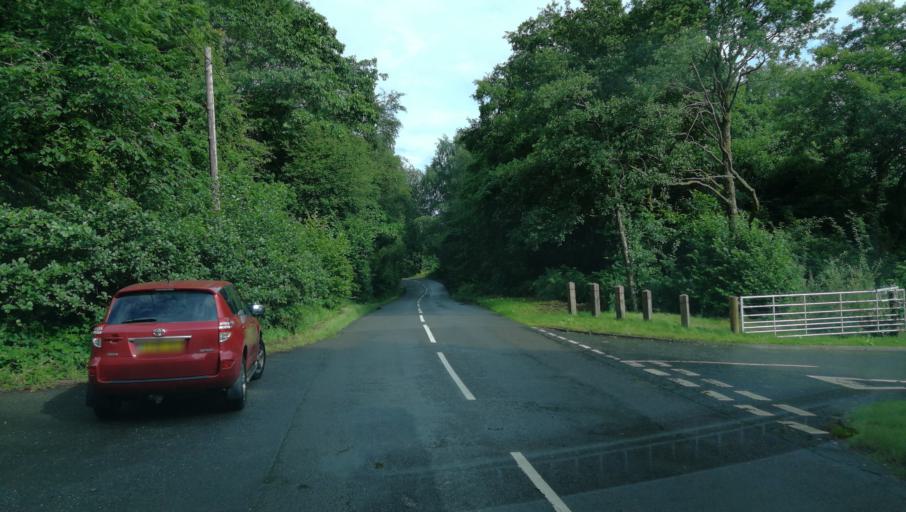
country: GB
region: Scotland
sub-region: Stirling
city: Callander
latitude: 56.2269
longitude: -4.3227
